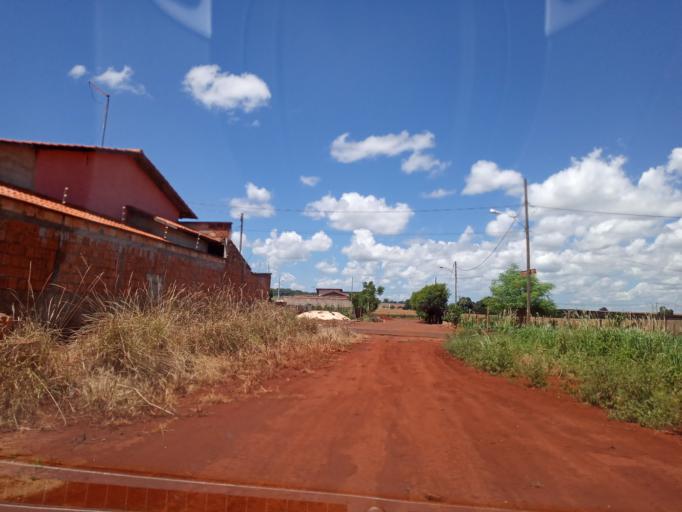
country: BR
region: Minas Gerais
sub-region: Centralina
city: Centralina
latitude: -18.5937
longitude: -49.2024
